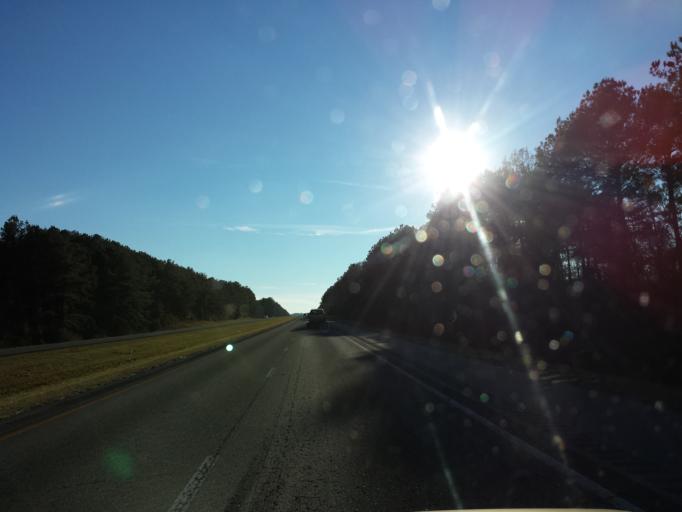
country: US
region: Alabama
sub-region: Hale County
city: Moundville
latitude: 33.0275
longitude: -87.7437
